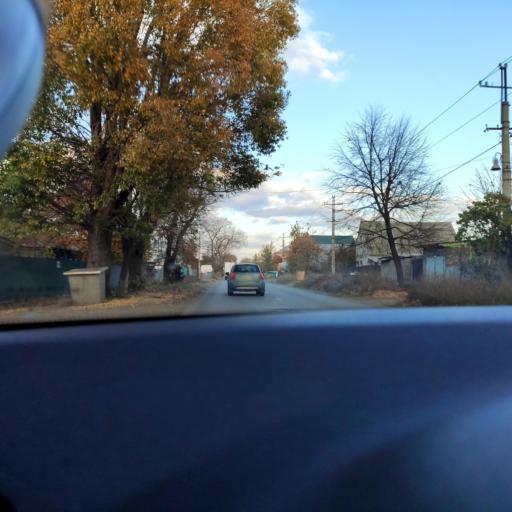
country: RU
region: Samara
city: Smyshlyayevka
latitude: 53.2368
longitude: 50.3244
